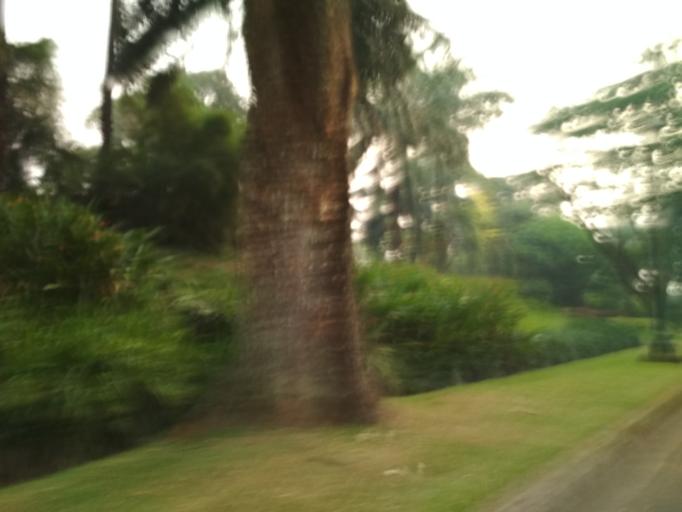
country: ID
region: West Java
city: Caringin
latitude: -6.6629
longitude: 106.8416
